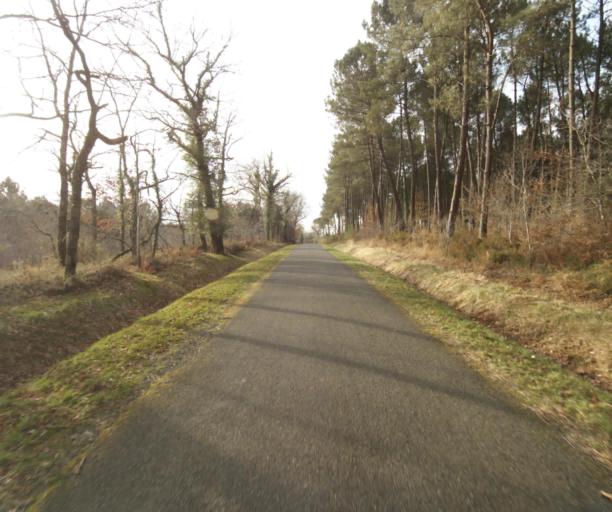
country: FR
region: Aquitaine
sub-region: Departement des Landes
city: Gabarret
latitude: 44.0099
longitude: 0.0564
